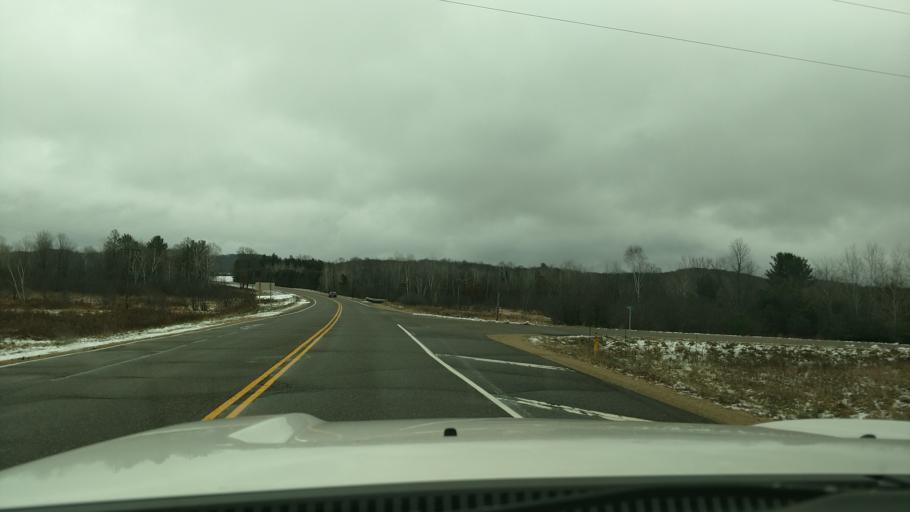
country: US
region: Wisconsin
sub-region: Dunn County
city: Tainter Lake
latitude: 45.1222
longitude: -91.8932
